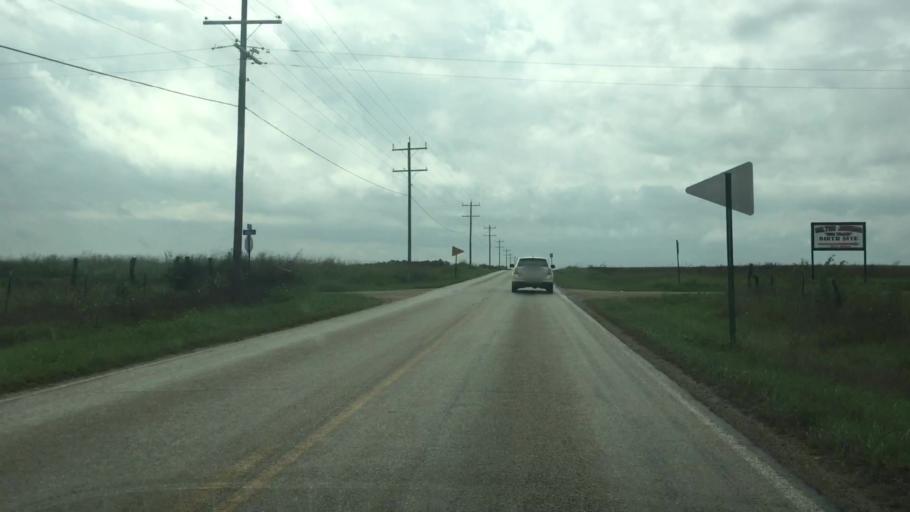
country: US
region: Kansas
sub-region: Allen County
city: Humboldt
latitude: 37.8495
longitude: -95.4369
